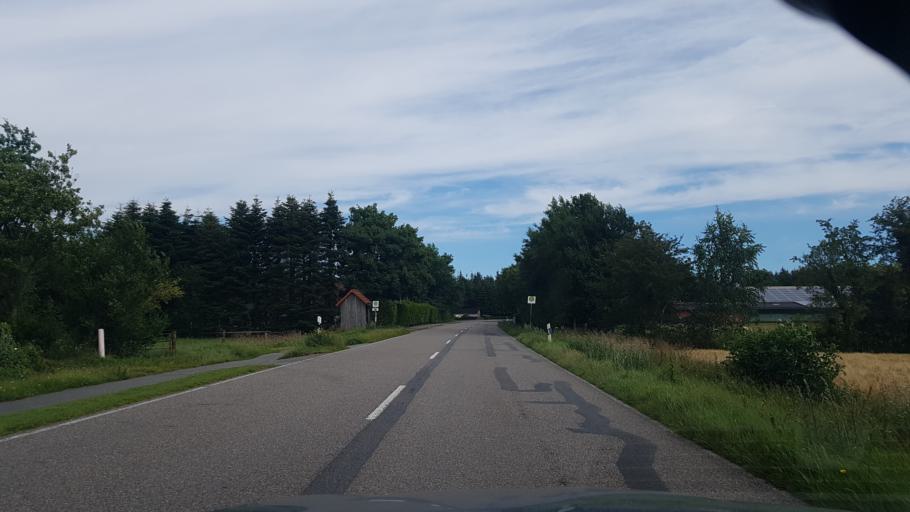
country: DE
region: Schleswig-Holstein
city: Ladelund
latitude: 54.8524
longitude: 9.0372
